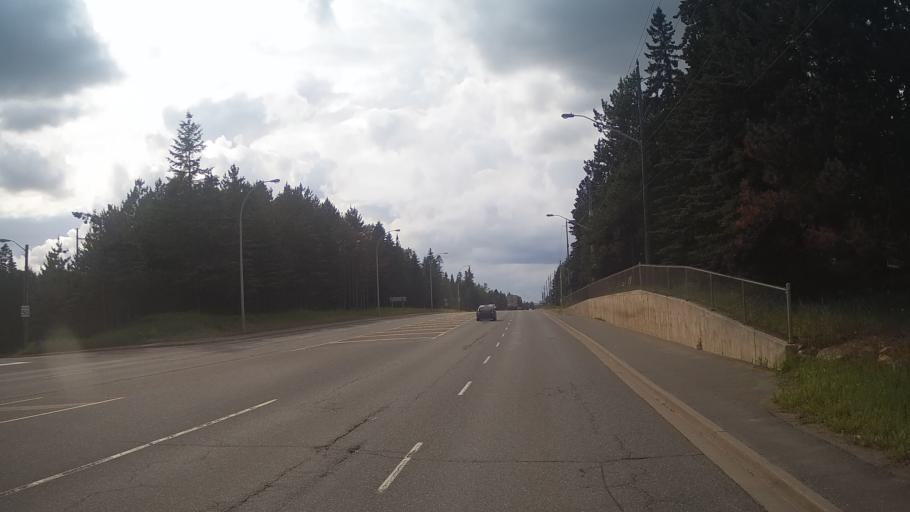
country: CA
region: Ontario
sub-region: Thunder Bay District
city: Thunder Bay
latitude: 48.4608
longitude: -89.2722
